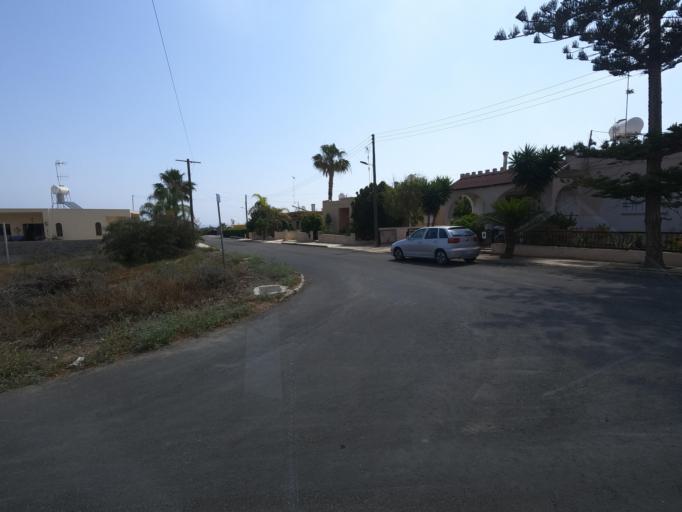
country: CY
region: Ammochostos
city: Deryneia
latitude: 35.0673
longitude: 33.9648
